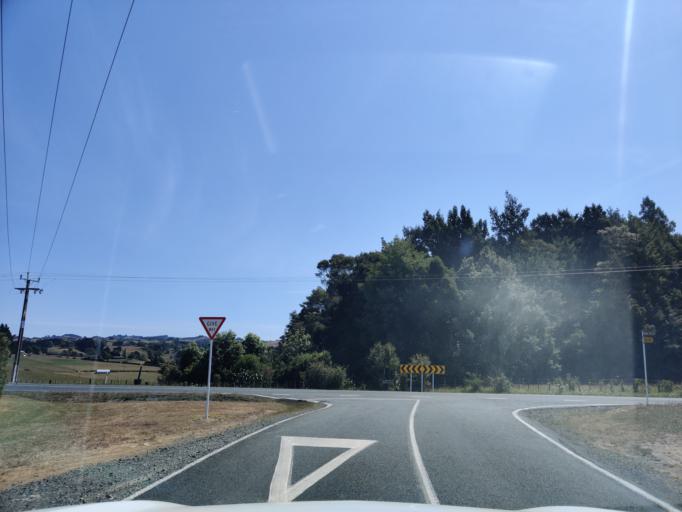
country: NZ
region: Auckland
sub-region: Auckland
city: Red Hill
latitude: -37.0691
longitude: 175.0709
